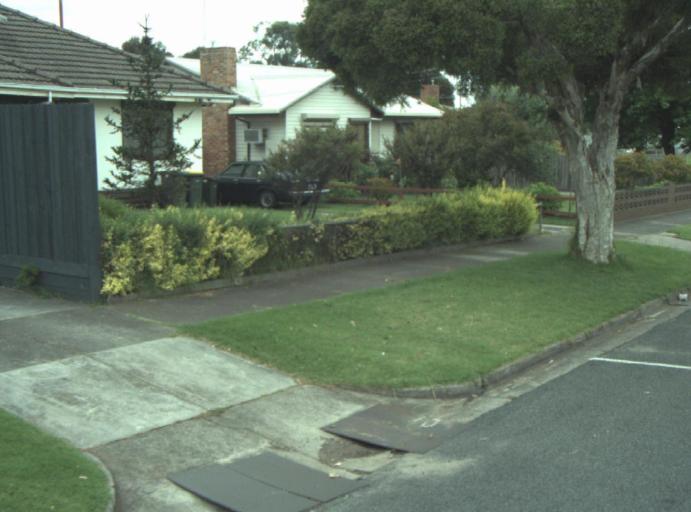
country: AU
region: Victoria
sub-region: Greater Geelong
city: East Geelong
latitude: -38.1675
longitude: 144.3726
